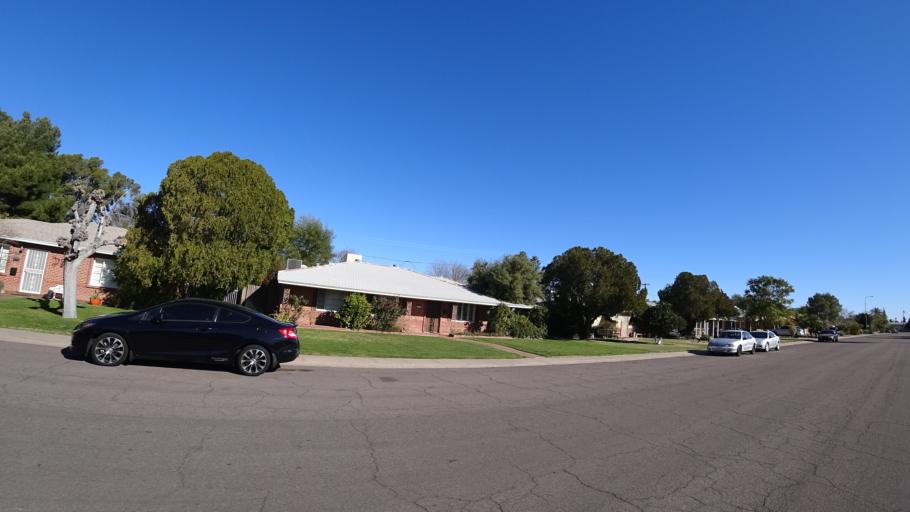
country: US
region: Arizona
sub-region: Maricopa County
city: Phoenix
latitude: 33.4975
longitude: -112.0341
